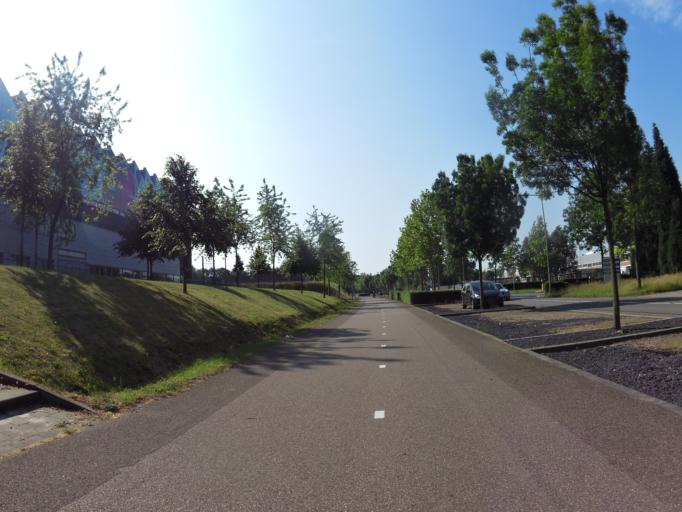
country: NL
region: Limburg
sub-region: Gemeente Simpelveld
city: Simpelveld
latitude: 50.8589
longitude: 6.0174
